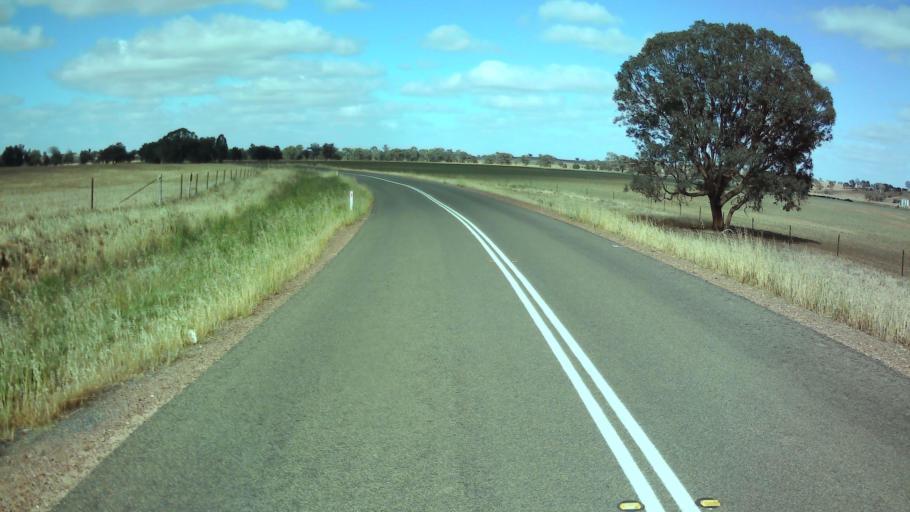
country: AU
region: New South Wales
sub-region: Weddin
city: Grenfell
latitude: -33.9782
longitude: 148.4212
